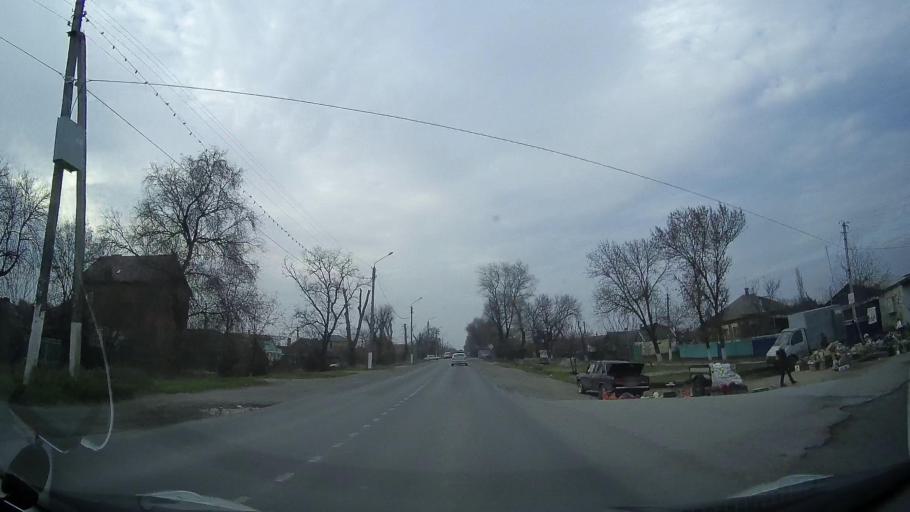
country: RU
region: Rostov
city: Ol'ginskaya
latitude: 47.1899
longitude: 39.9485
